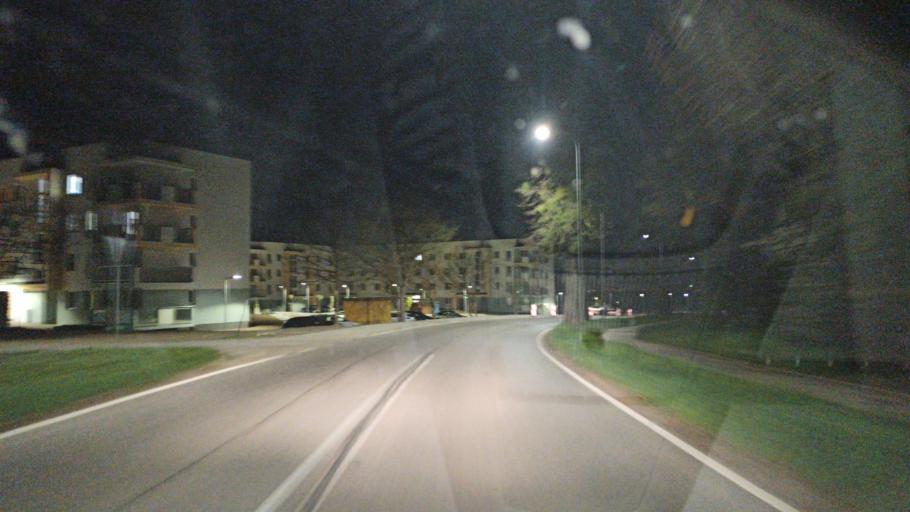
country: PL
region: Warmian-Masurian Voivodeship
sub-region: Powiat elblaski
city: Gronowo Gorne
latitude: 54.1569
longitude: 19.4456
